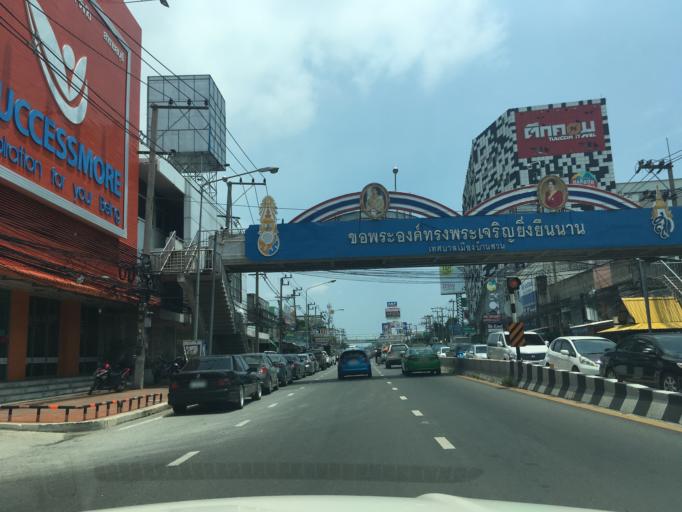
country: TH
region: Chon Buri
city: Chon Buri
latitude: 13.3416
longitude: 100.9747
